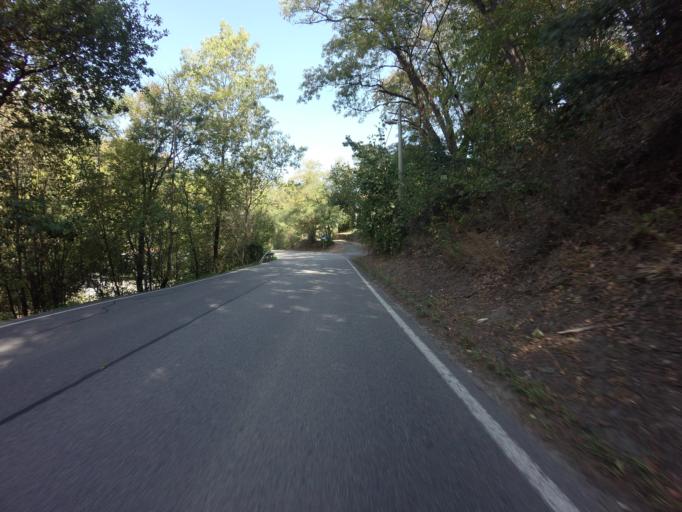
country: CZ
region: Central Bohemia
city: Kamenny Privoz
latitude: 49.8752
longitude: 14.5017
